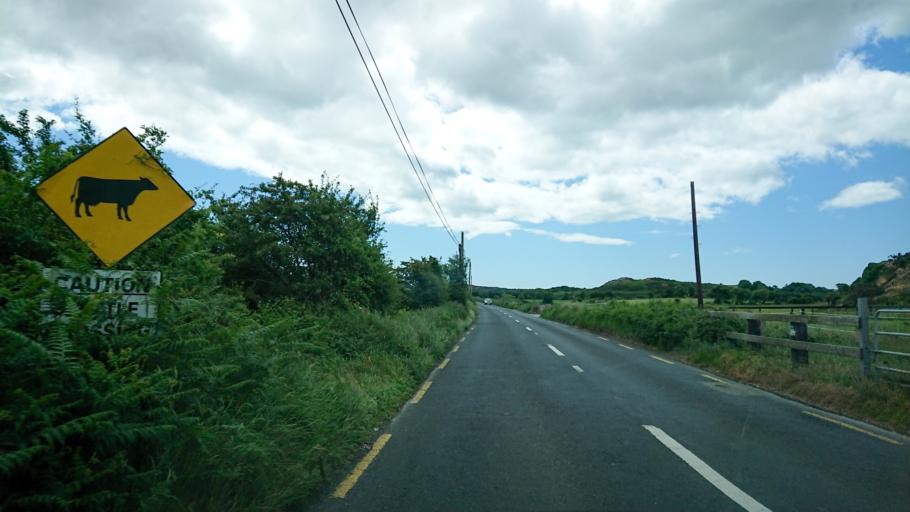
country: IE
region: Munster
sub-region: Waterford
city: Tra Mhor
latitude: 52.1888
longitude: -7.1799
